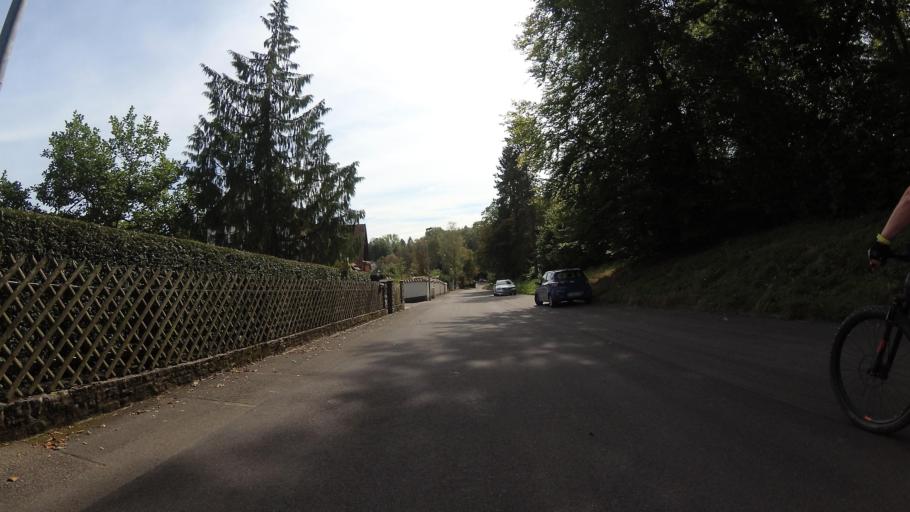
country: DE
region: Saarland
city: Sankt Ingbert
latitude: 49.3009
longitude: 7.1082
